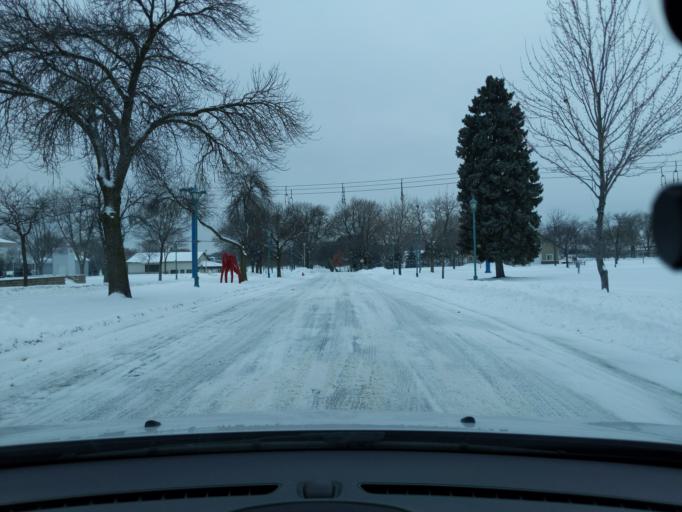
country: US
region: Minnesota
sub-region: Ramsey County
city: Falcon Heights
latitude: 44.9845
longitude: -93.1693
